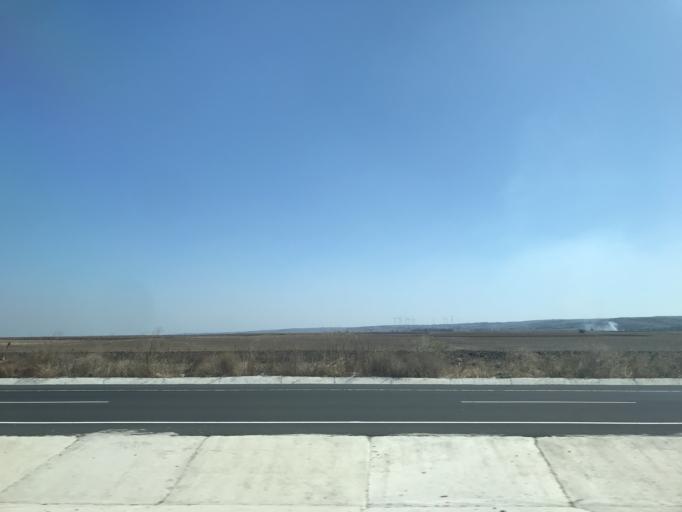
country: TR
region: Tekirdag
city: Muratli
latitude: 41.1675
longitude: 27.5337
